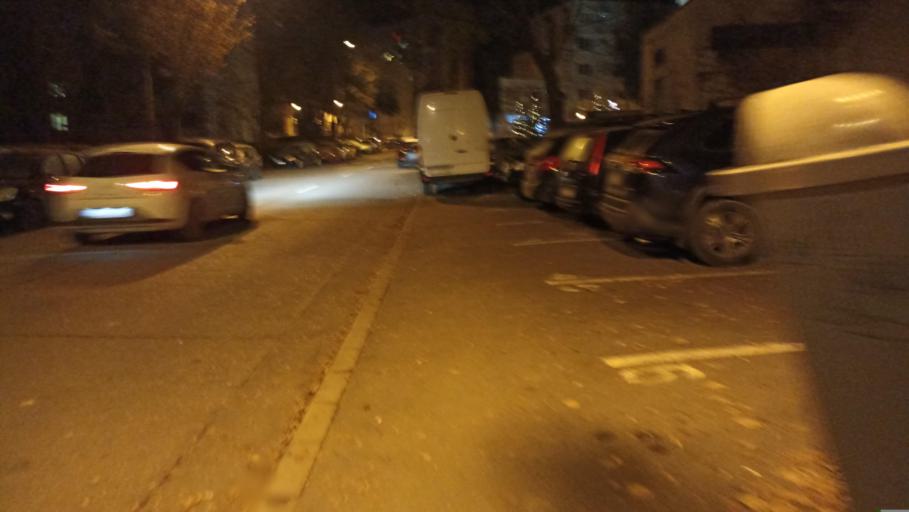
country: RO
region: Cluj
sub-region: Municipiul Cluj-Napoca
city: Cluj-Napoca
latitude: 46.7513
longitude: 23.5509
